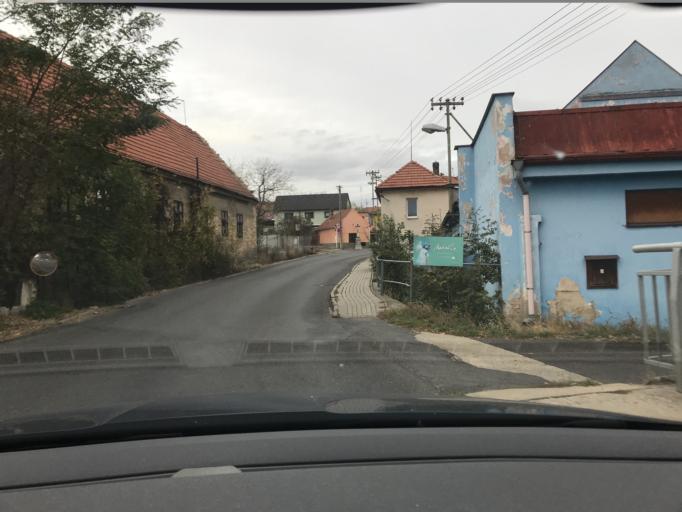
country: CZ
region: Ustecky
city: Roudnice nad Labem
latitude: 50.4221
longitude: 14.2277
